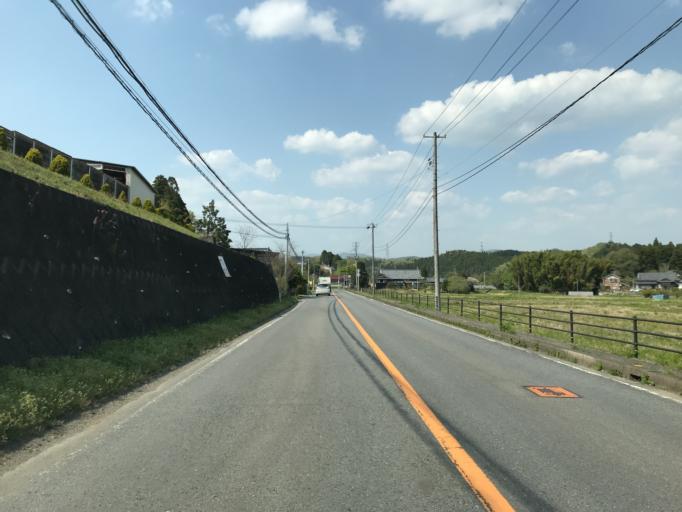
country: JP
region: Fukushima
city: Iwaki
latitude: 36.9451
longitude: 140.7682
